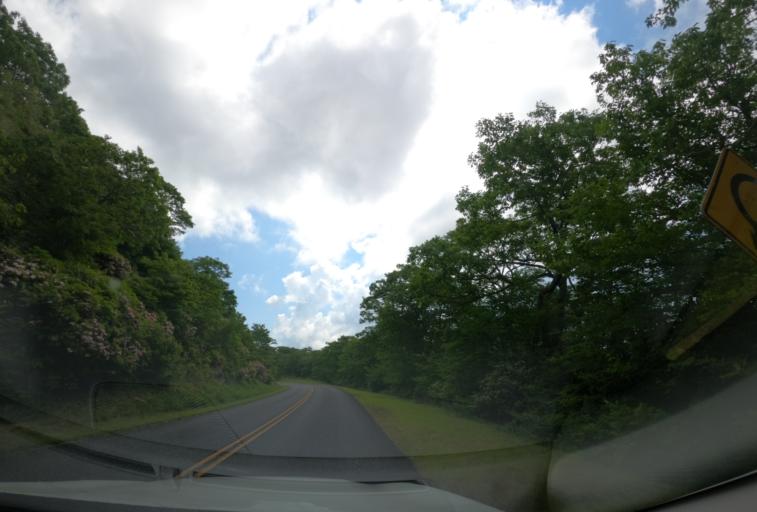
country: US
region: North Carolina
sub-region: Haywood County
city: Hazelwood
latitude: 35.4124
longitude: -83.0414
